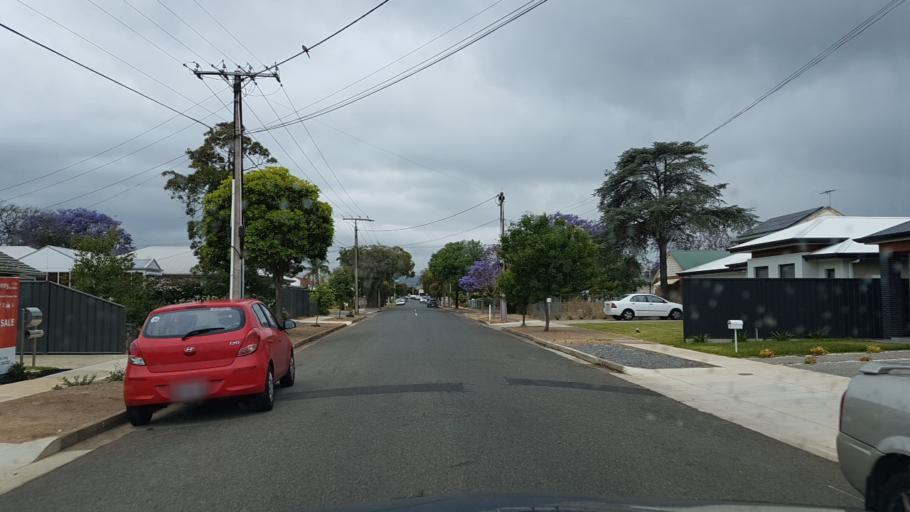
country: AU
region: South Australia
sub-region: Marion
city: South Plympton
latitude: -34.9766
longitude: 138.5527
